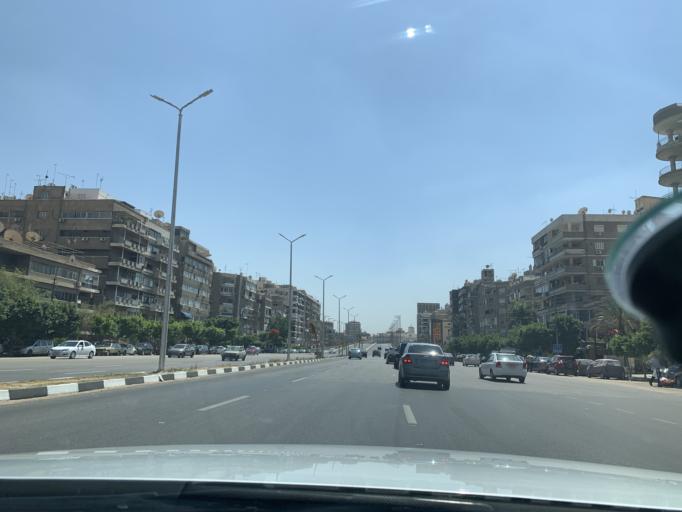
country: EG
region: Muhafazat al Qahirah
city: Cairo
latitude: 30.0894
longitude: 31.3390
